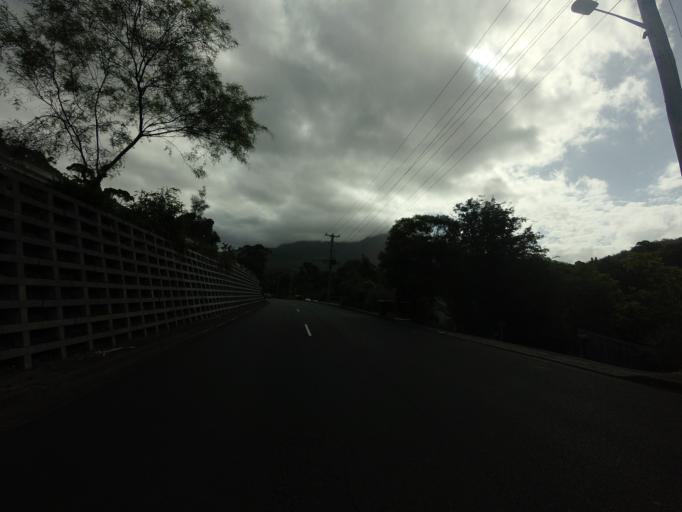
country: AU
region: Tasmania
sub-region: Hobart
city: Dynnyrne
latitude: -42.8983
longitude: 147.2858
